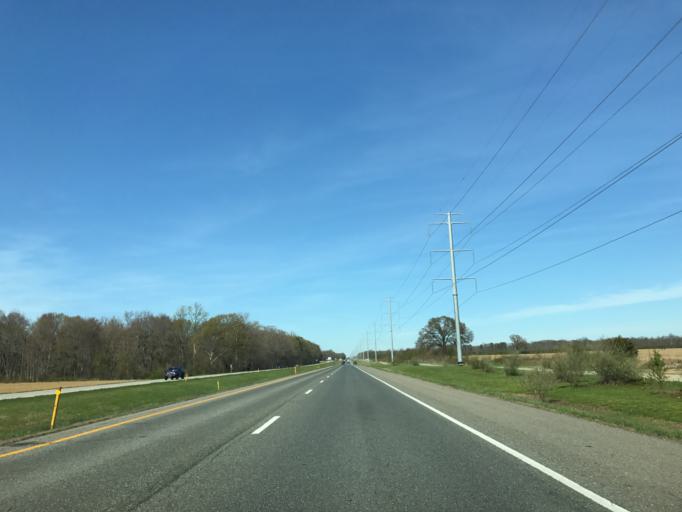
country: US
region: Maryland
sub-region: Queen Anne's County
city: Centreville
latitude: 39.0546
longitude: -76.0006
